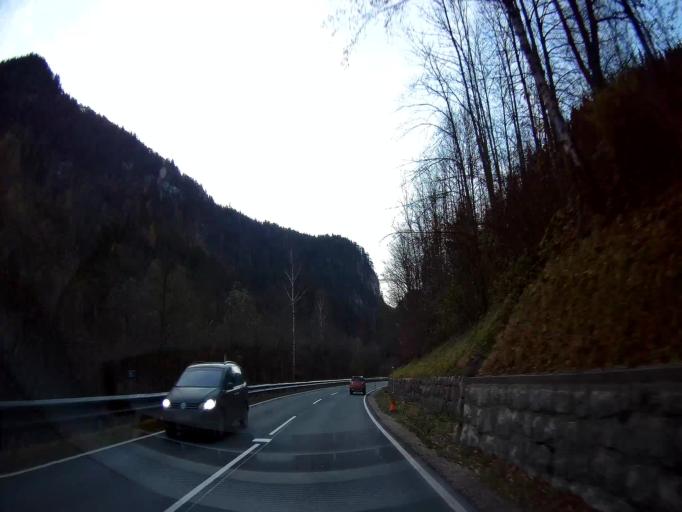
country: AT
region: Salzburg
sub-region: Politischer Bezirk Zell am See
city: Unken
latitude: 47.6434
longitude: 12.7238
